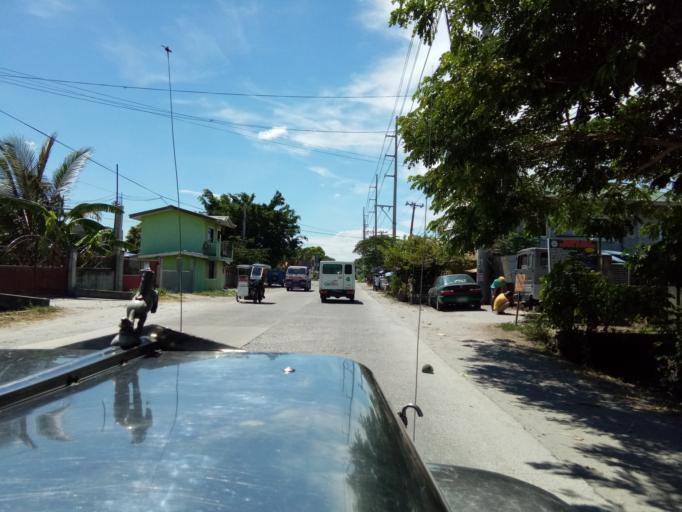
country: PH
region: Calabarzon
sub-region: Province of Cavite
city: General Trias
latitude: 14.3681
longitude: 120.8912
